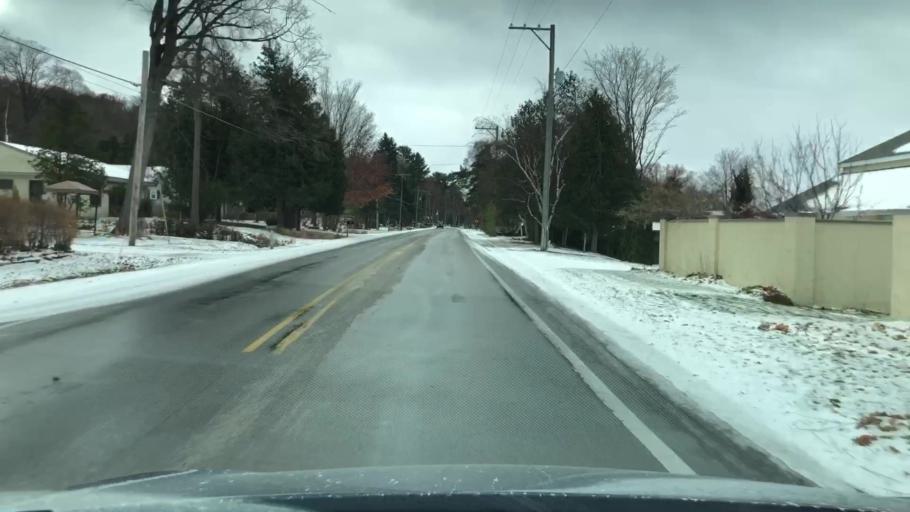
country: US
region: Michigan
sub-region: Grand Traverse County
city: Traverse City
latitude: 44.7958
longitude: -85.5854
